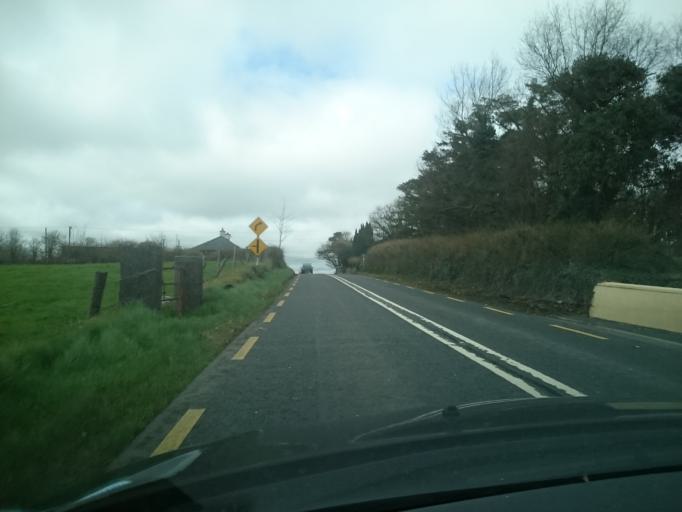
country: IE
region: Connaught
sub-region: Maigh Eo
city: Castlebar
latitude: 53.8139
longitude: -9.1551
